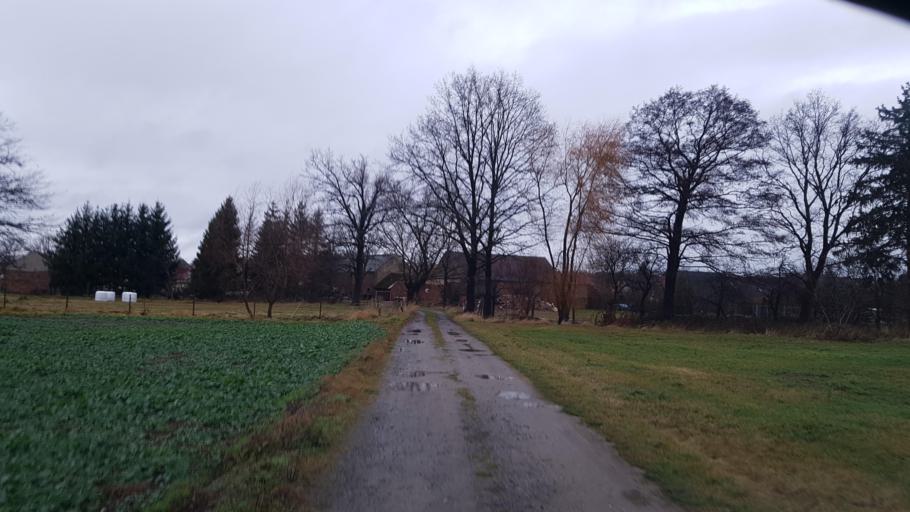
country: DE
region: Brandenburg
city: Luckau
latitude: 51.8382
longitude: 13.6920
